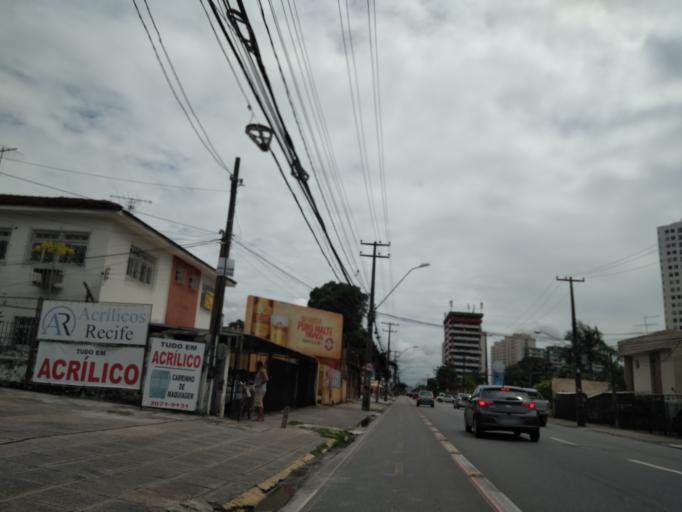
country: BR
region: Pernambuco
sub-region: Recife
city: Recife
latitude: -8.1121
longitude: -34.9028
